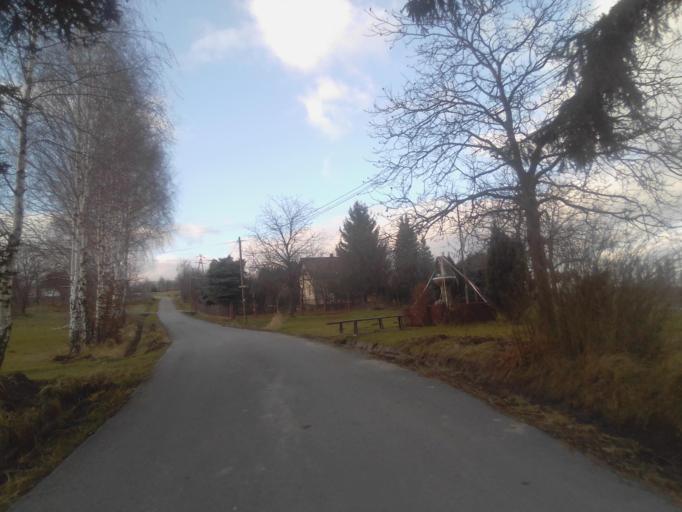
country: PL
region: Subcarpathian Voivodeship
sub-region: Powiat strzyzowski
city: Babica
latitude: 49.9422
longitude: 21.8908
